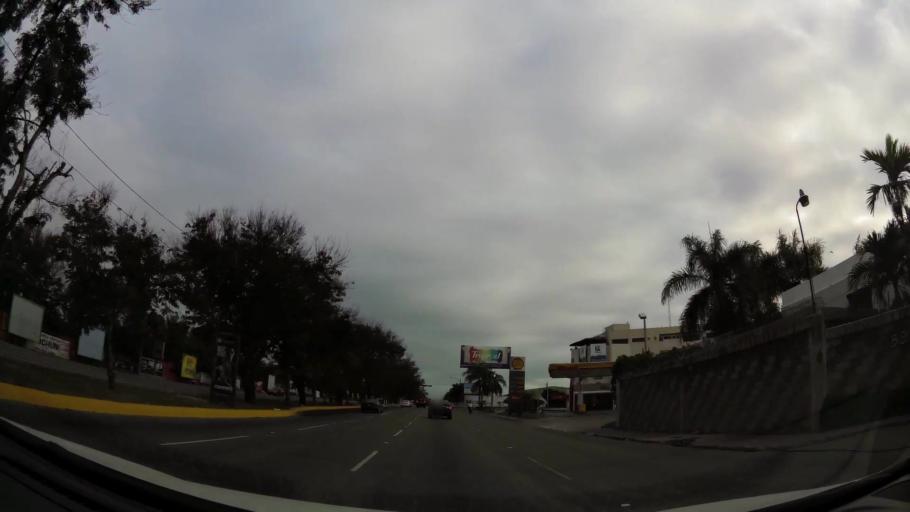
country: DO
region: Nacional
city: Bella Vista
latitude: 18.4686
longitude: -69.9684
